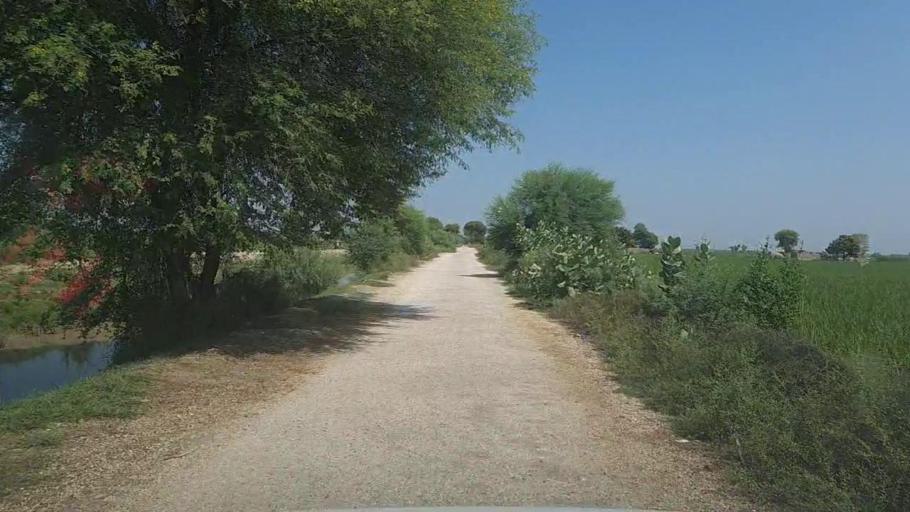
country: PK
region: Sindh
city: Kandhkot
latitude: 28.3015
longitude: 69.2386
